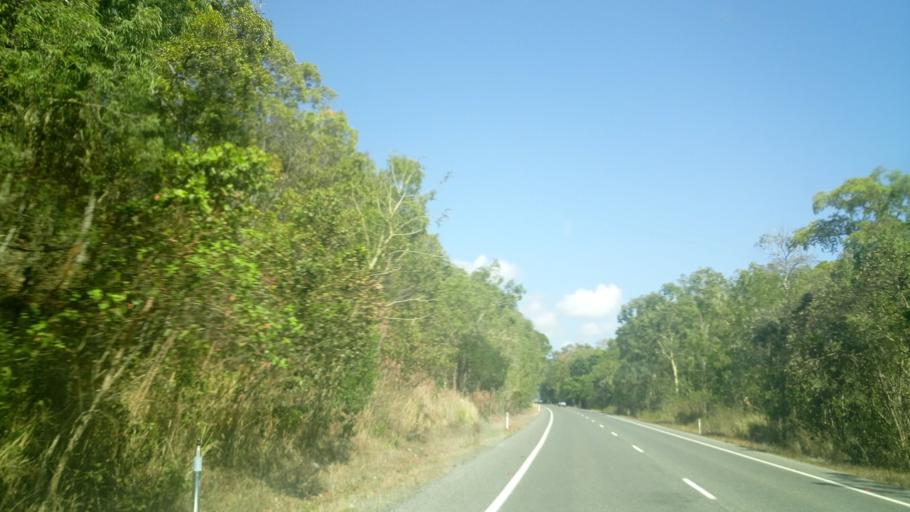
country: AU
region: Queensland
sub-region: Cairns
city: Port Douglas
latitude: -16.5620
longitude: 145.4975
